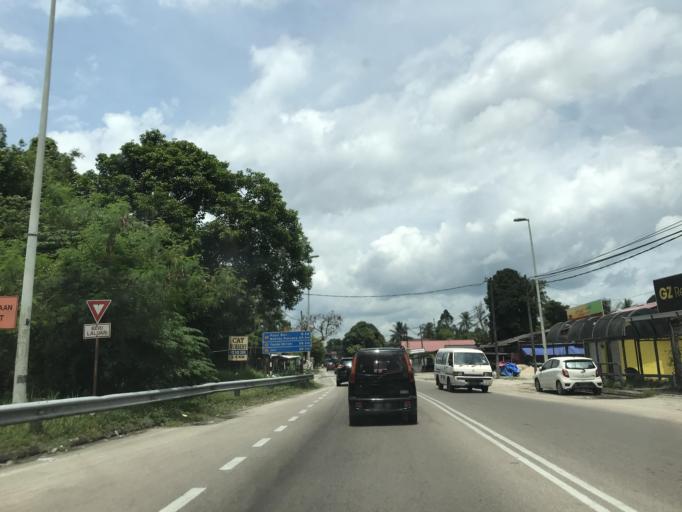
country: MY
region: Kelantan
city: Pasir Mas
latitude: 6.0633
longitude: 102.2046
